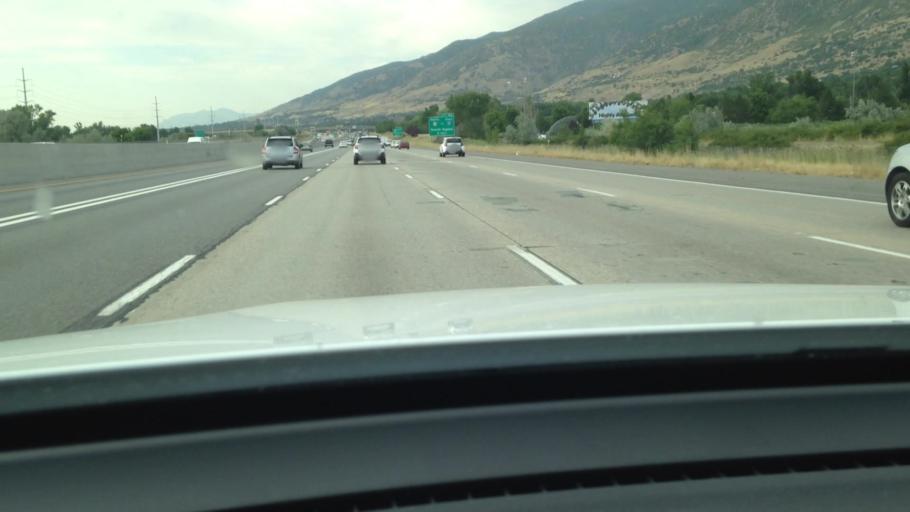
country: US
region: Utah
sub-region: Davis County
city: Farmington
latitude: 40.9537
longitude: -111.8908
